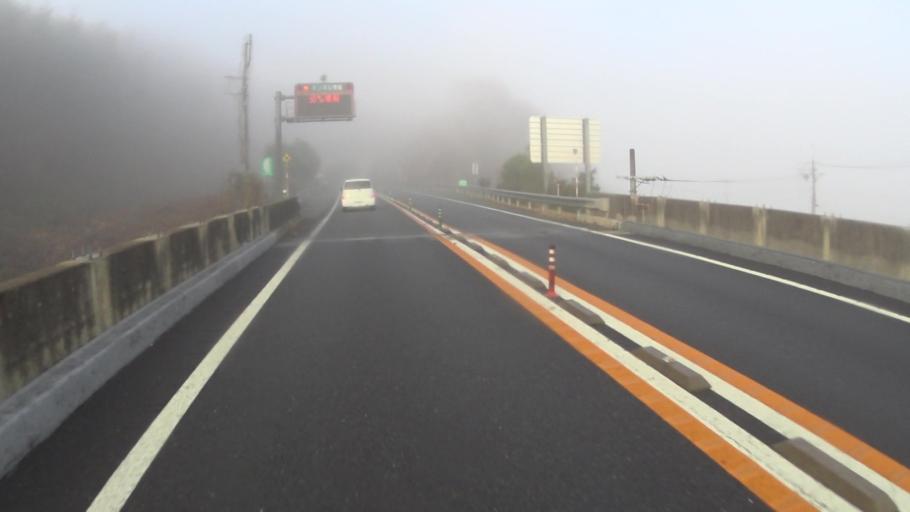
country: JP
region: Kyoto
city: Kameoka
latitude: 35.1275
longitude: 135.4709
